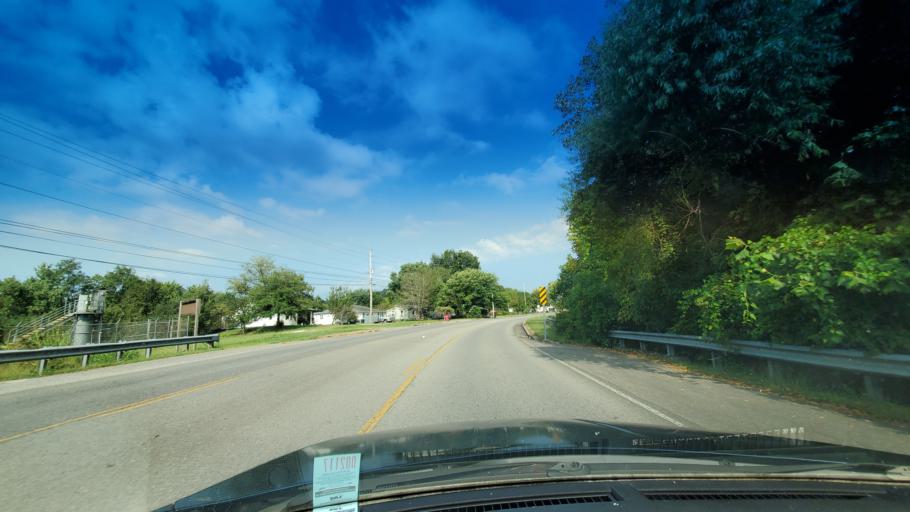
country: US
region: Tennessee
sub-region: Smith County
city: South Carthage
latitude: 36.2448
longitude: -85.9463
